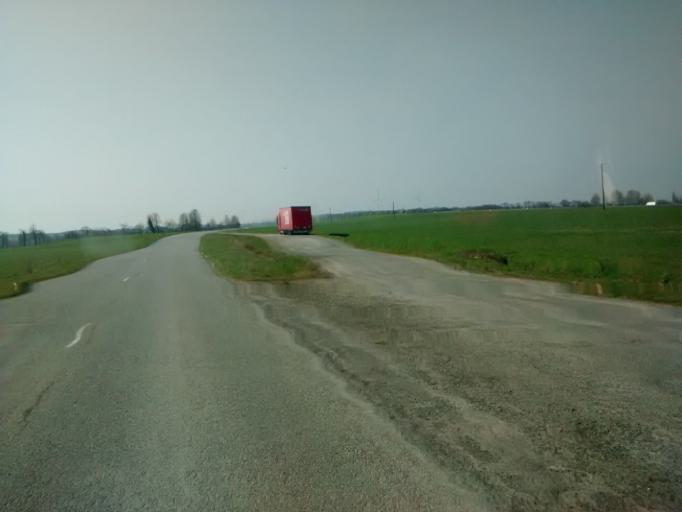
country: FR
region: Brittany
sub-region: Departement d'Ille-et-Vilaine
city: Maxent
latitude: 48.0264
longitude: -2.0197
